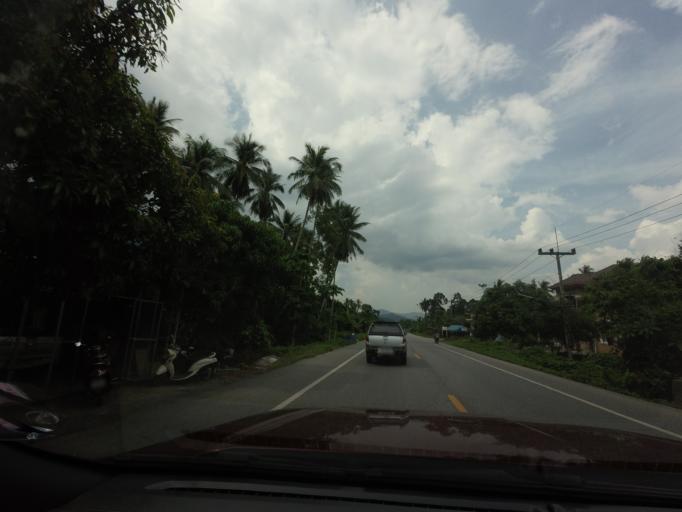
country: TH
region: Yala
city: Ban Nang Sata
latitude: 6.2680
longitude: 101.2792
